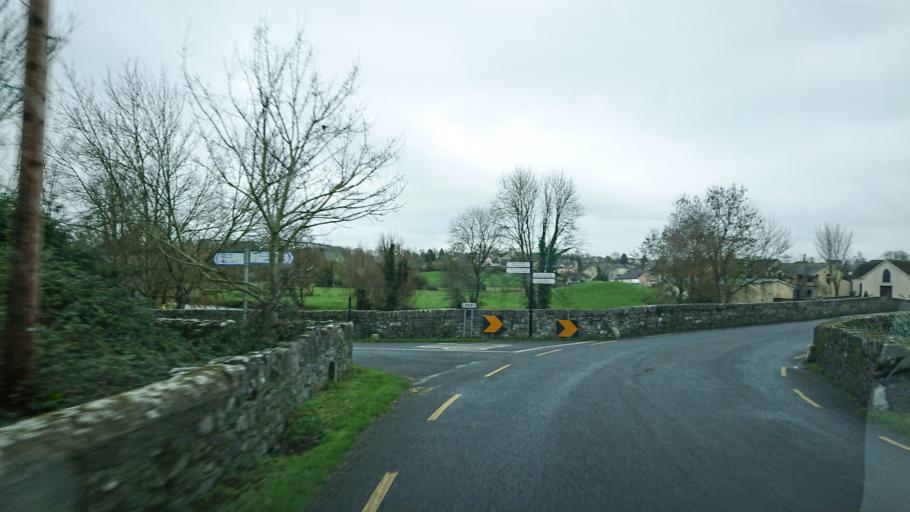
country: IE
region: Leinster
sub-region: Kilkenny
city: Kilkenny
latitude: 52.5430
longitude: -7.2723
